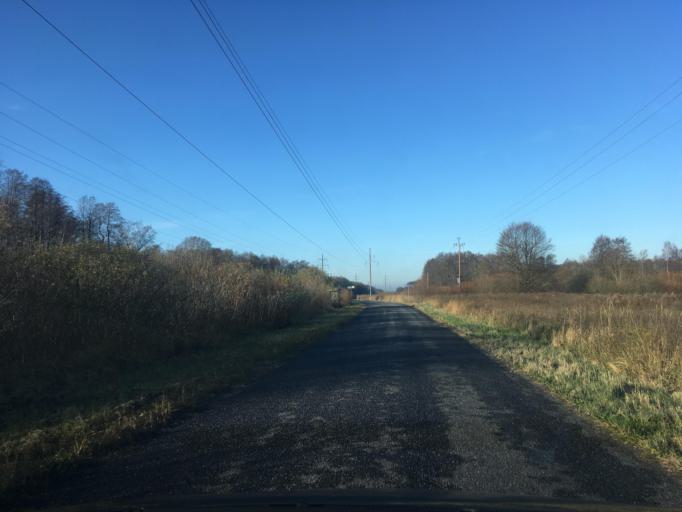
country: EE
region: Harju
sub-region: Maardu linn
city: Maardu
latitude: 59.4777
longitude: 25.1133
